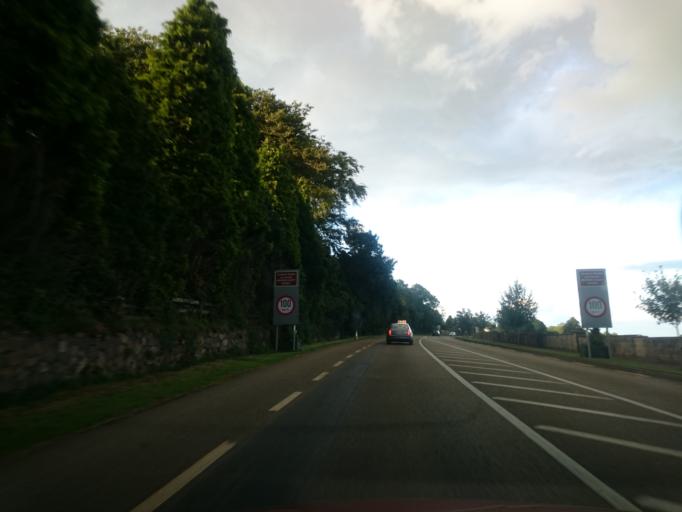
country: IE
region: Leinster
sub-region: Loch Garman
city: Ferns
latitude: 52.5930
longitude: -6.4886
